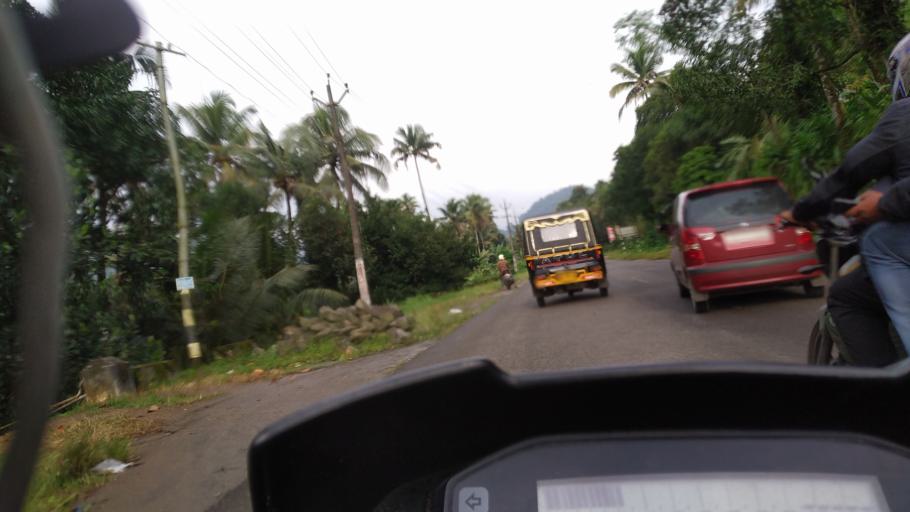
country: IN
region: Kerala
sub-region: Idukki
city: Kuttampuzha
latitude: 10.0519
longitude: 76.7408
